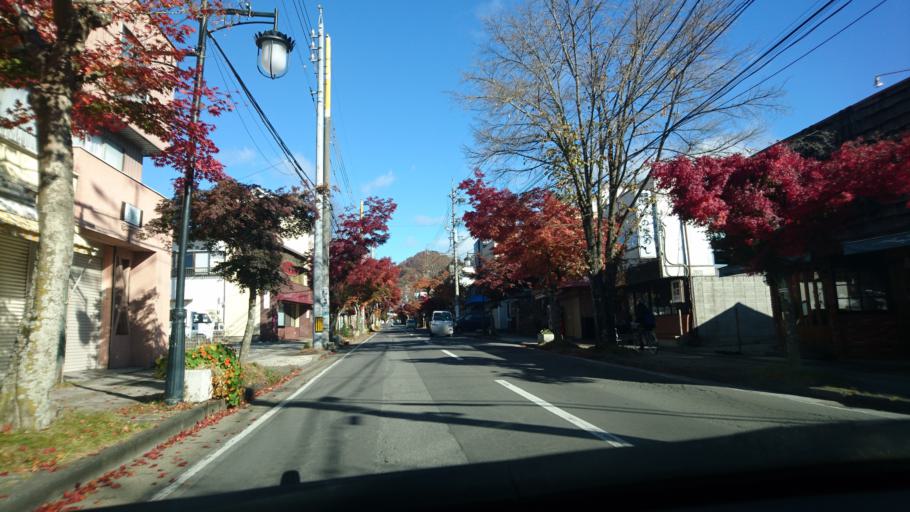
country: JP
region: Nagano
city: Saku
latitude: 36.3544
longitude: 138.6341
